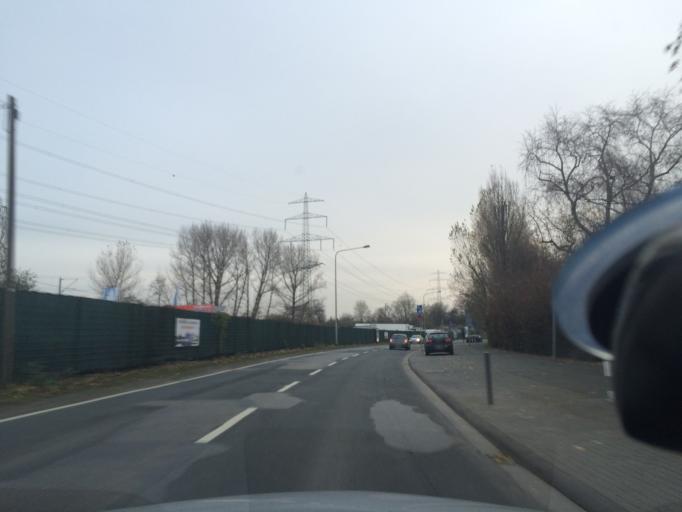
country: DE
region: Hesse
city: Niederrad
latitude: 50.1077
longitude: 8.6059
